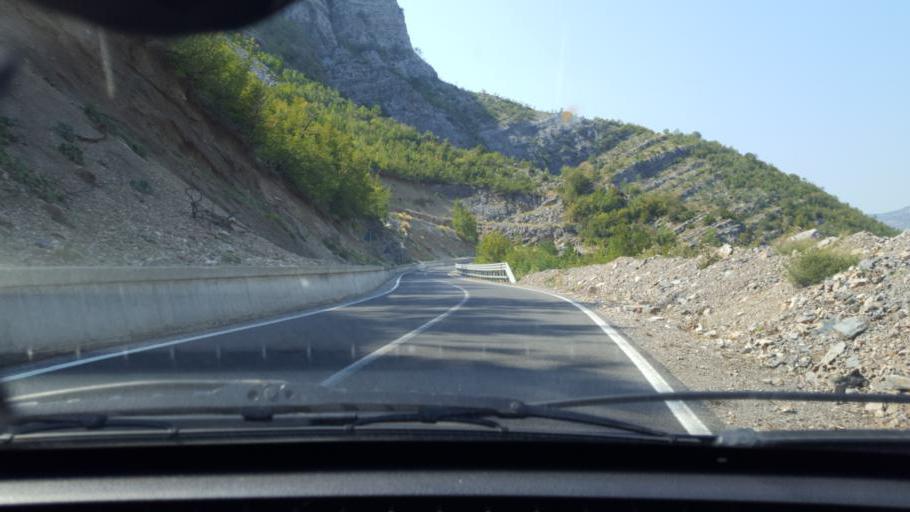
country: AL
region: Shkoder
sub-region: Rrethi i Malesia e Madhe
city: Kastrat
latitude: 42.4147
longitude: 19.4991
